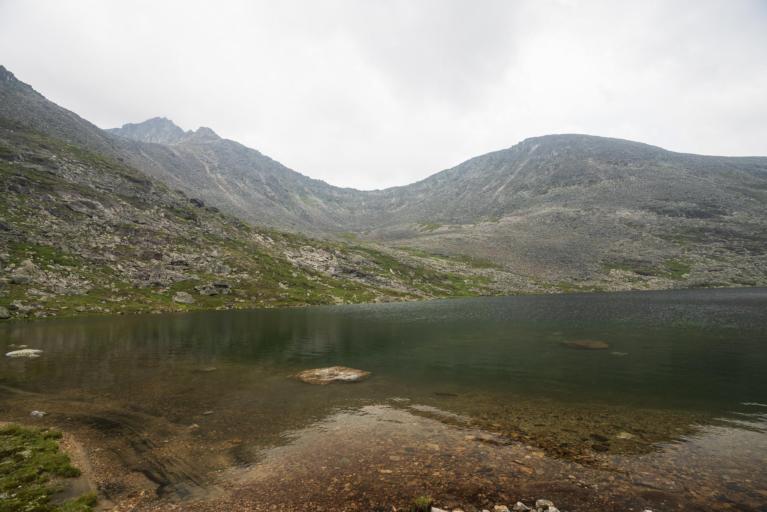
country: RU
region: Transbaikal Territory
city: Kuanda
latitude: 56.7750
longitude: 116.7058
